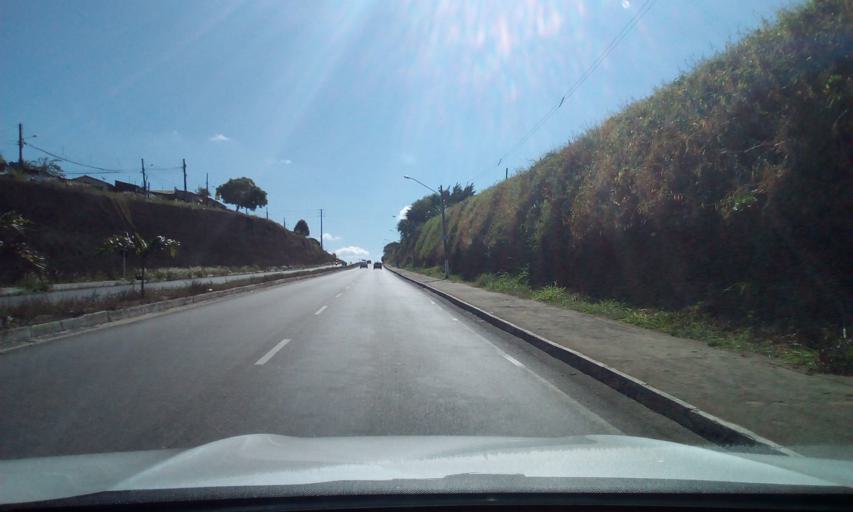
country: BR
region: Paraiba
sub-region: Bayeux
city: Bayeux
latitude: -7.1327
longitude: -34.9341
